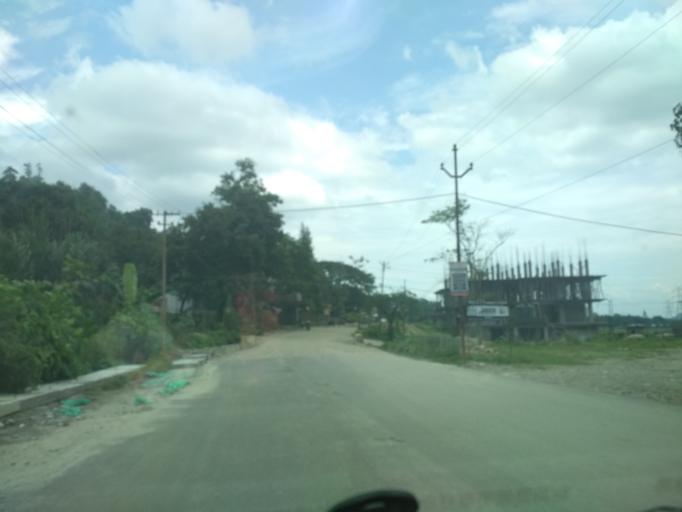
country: IN
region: Arunachal Pradesh
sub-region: Papum Pare
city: Naharlagun
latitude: 27.1430
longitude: 93.7584
